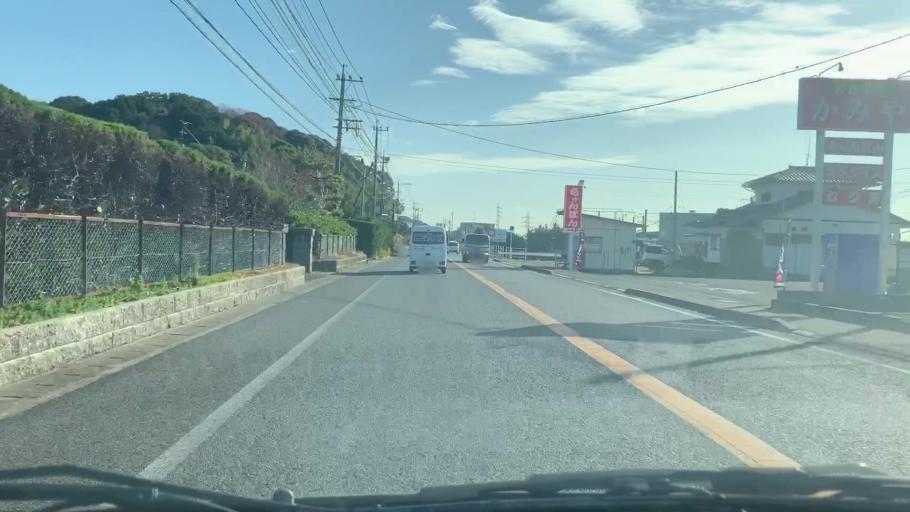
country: JP
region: Saga Prefecture
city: Takeocho-takeo
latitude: 33.2159
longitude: 130.0878
